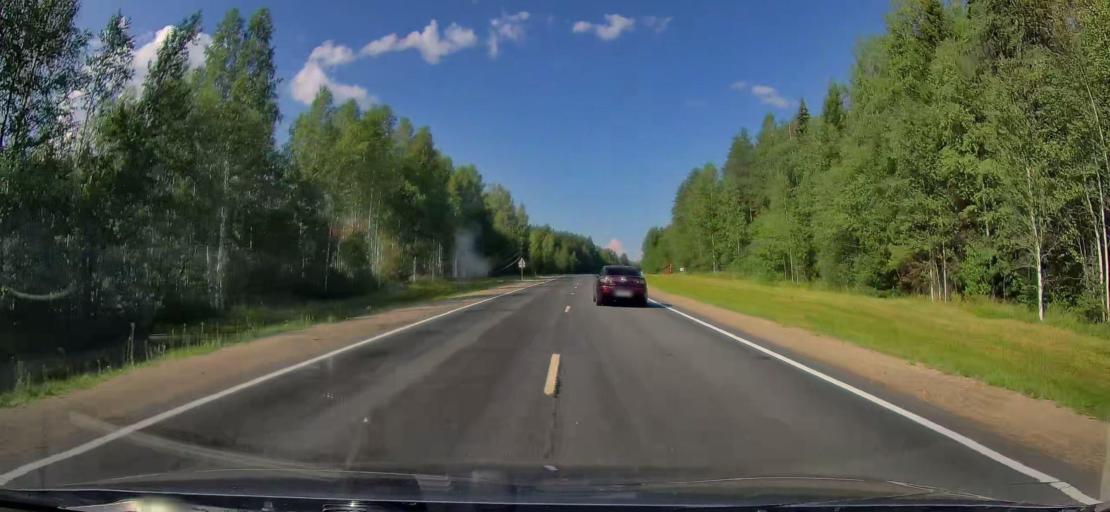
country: RU
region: Vologda
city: Verkhovazh'ye
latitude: 60.6711
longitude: 41.8042
